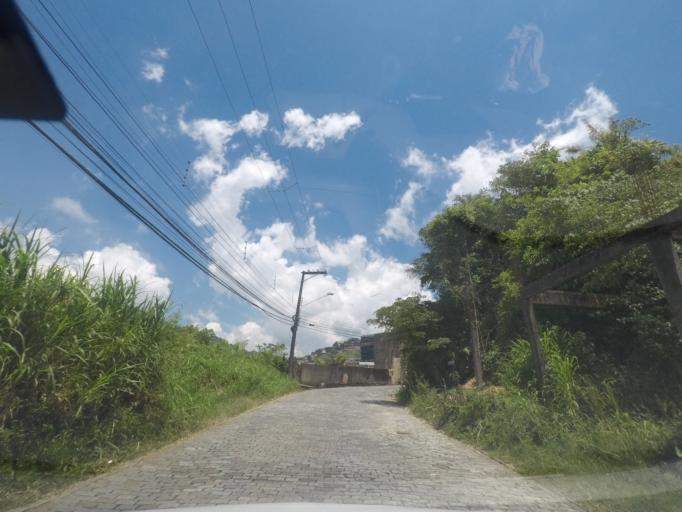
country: BR
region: Rio de Janeiro
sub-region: Petropolis
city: Petropolis
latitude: -22.5341
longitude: -43.1724
